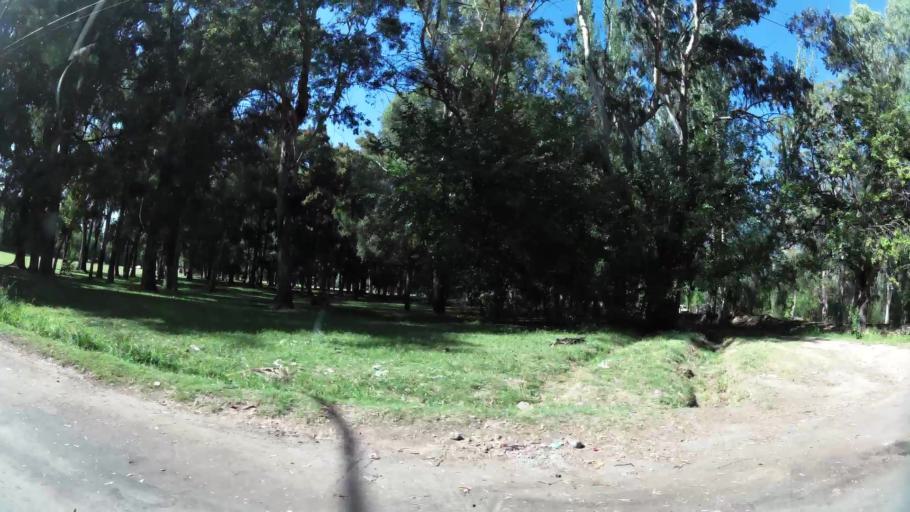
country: AR
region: Mendoza
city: Mendoza
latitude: -32.8919
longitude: -68.8747
